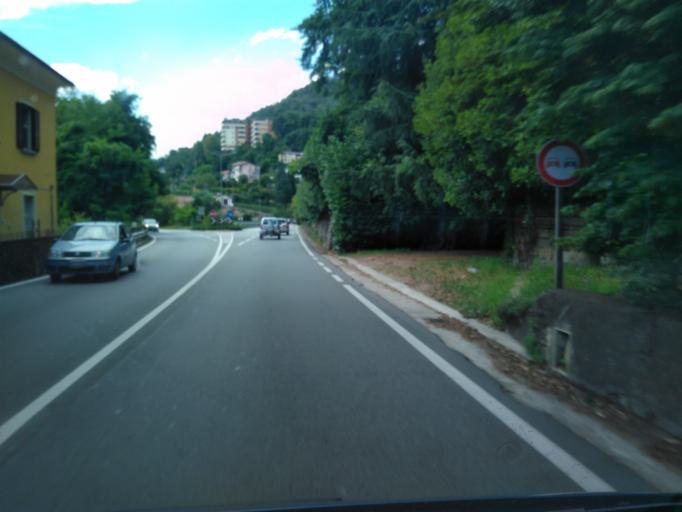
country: IT
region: Piedmont
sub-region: Provincia Verbano-Cusio-Ossola
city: Santino
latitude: 45.9356
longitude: 8.5246
